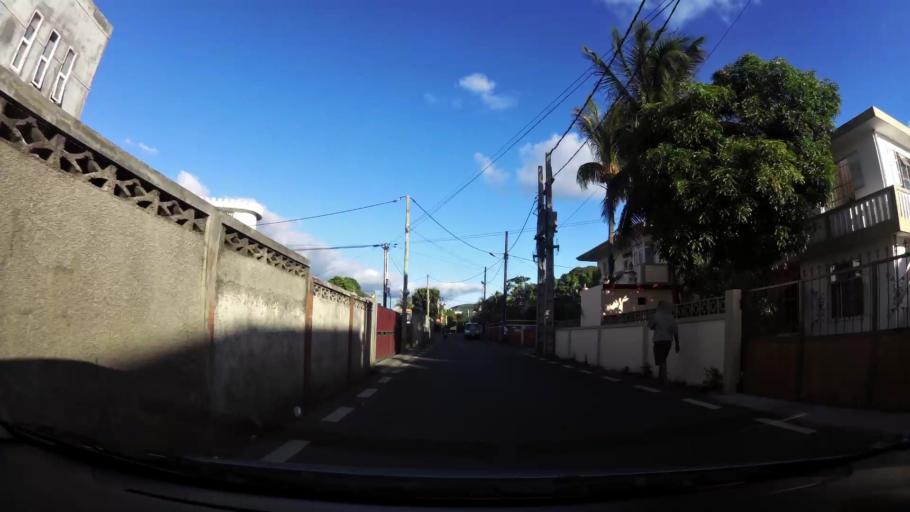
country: MU
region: Plaines Wilhems
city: Quatre Bornes
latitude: -20.2520
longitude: 57.4711
